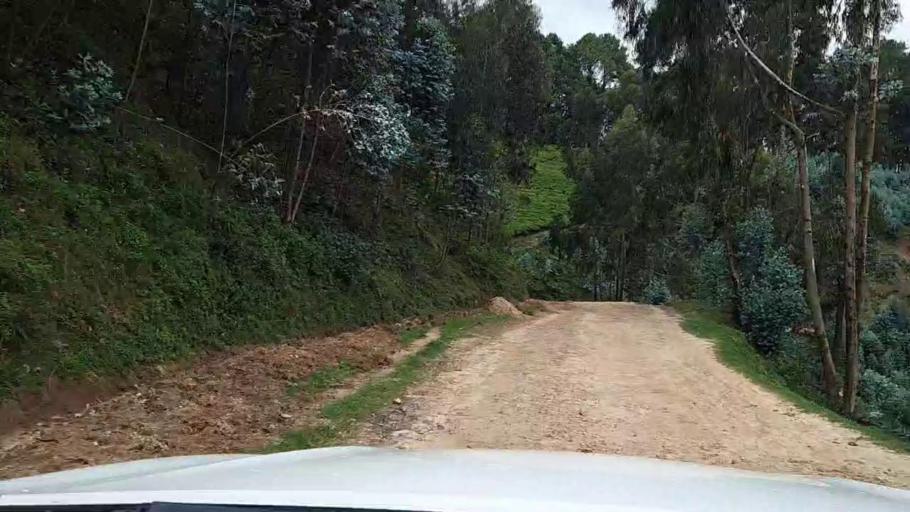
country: RW
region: Western Province
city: Kibuye
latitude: -2.2892
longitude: 29.3731
